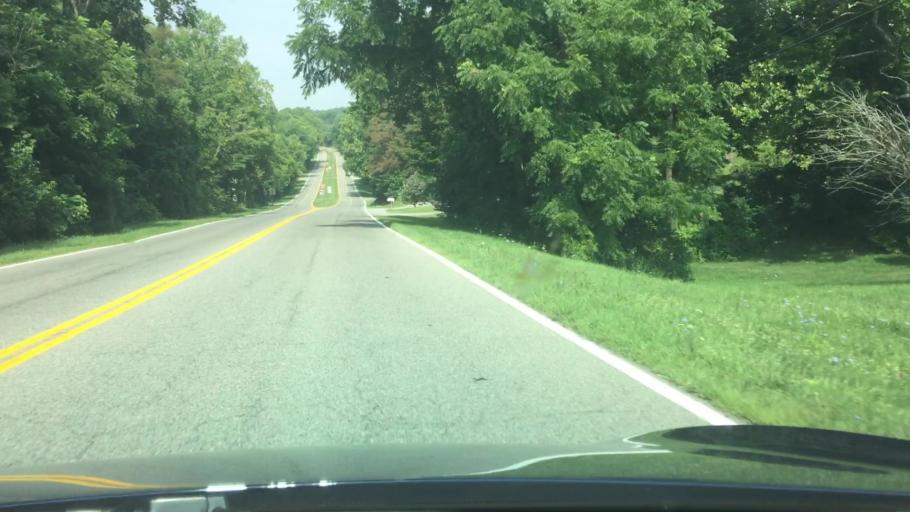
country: US
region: Virginia
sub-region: Pulaski County
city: Pulaski
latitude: 36.9495
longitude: -80.8977
